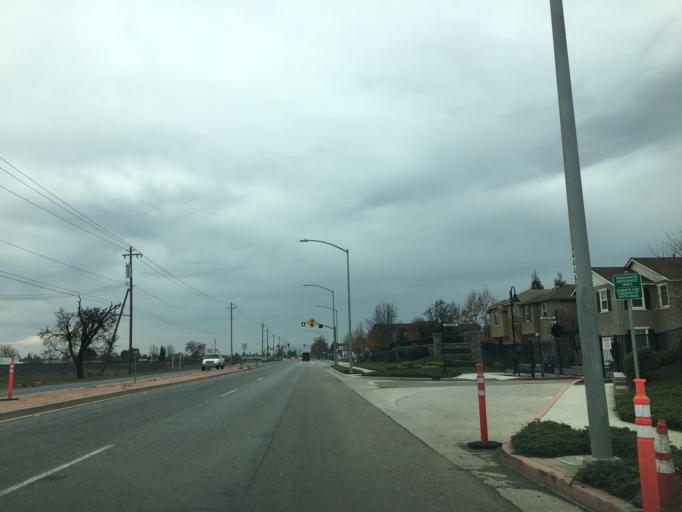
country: US
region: California
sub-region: Santa Clara County
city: Gilroy
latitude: 37.0340
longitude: -121.5824
